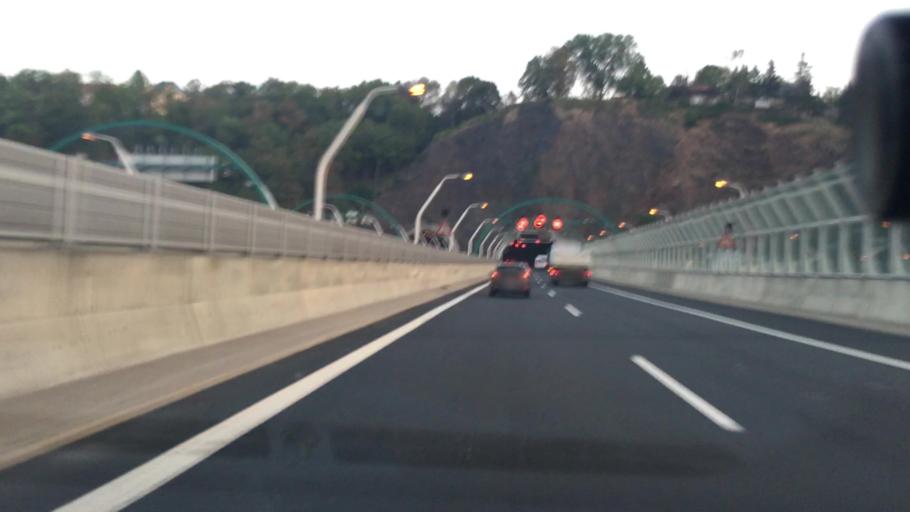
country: DE
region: Saxony
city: Bannewitz
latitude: 51.0200
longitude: 13.6951
